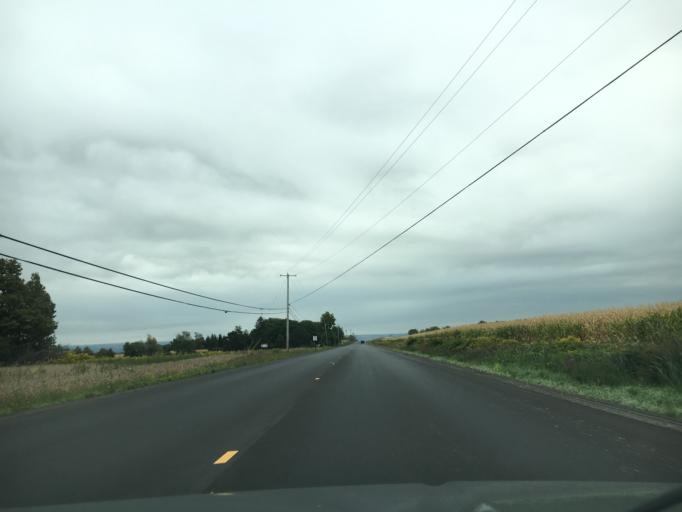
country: US
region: New York
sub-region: Cayuga County
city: Union Springs
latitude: 42.6811
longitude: -76.8085
